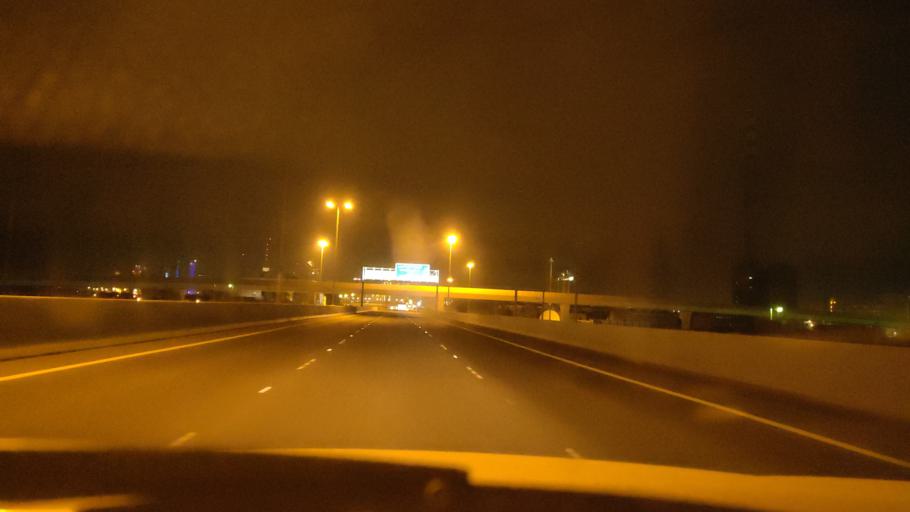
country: KW
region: Al Asimah
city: Ash Shamiyah
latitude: 29.3397
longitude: 47.9435
